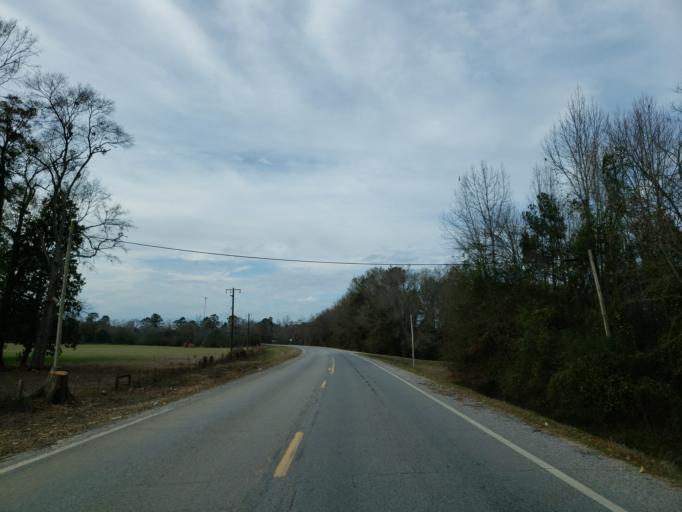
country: US
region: Mississippi
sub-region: Clarke County
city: Quitman
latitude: 31.8706
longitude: -88.7033
